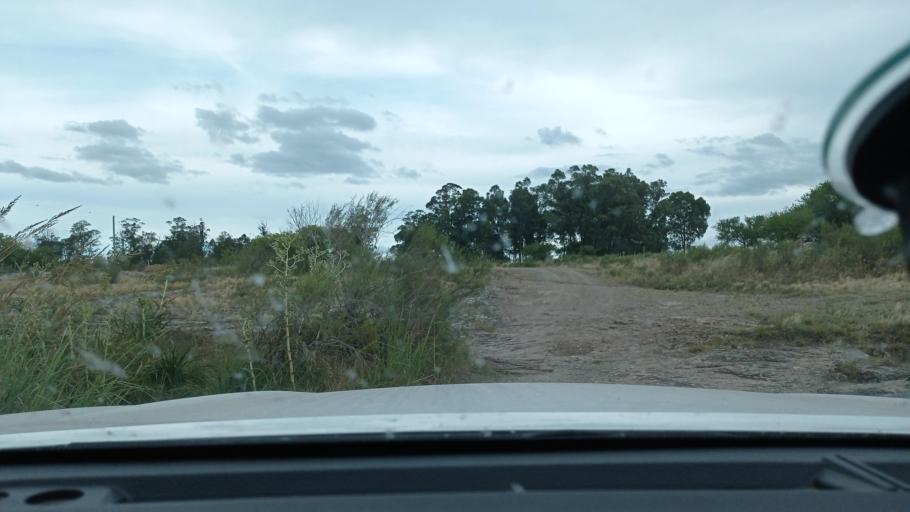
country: UY
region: Florida
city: Casupa
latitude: -34.1432
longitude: -55.7979
